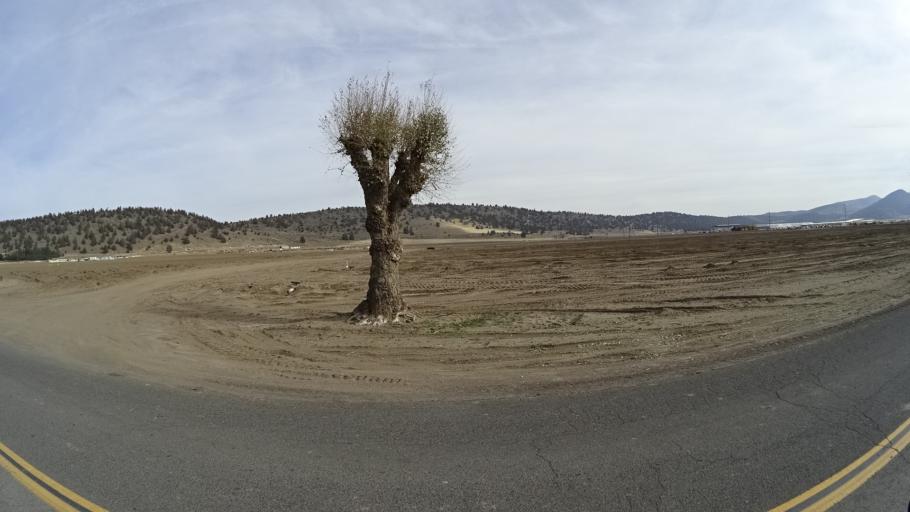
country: US
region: Oregon
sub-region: Klamath County
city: Klamath Falls
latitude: 41.9625
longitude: -121.9116
